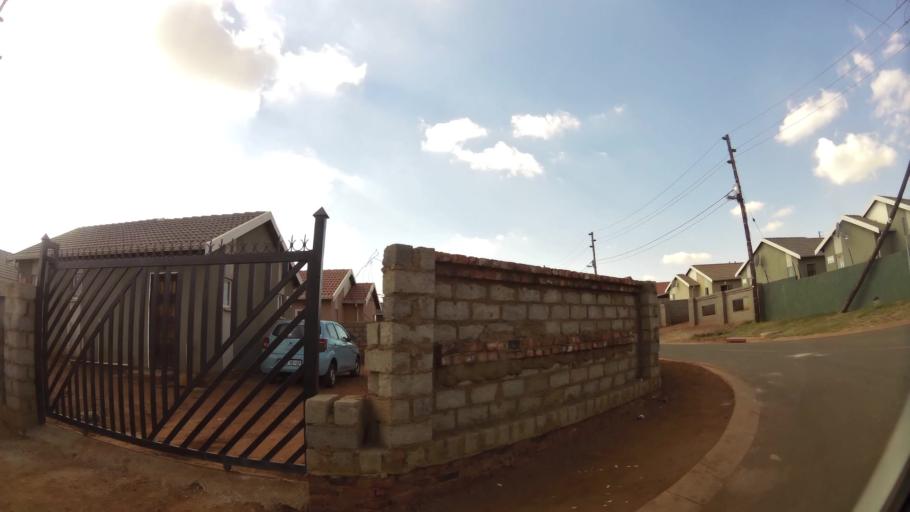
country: ZA
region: Gauteng
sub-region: City of Tshwane Metropolitan Municipality
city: Cullinan
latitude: -25.6891
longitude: 28.4064
